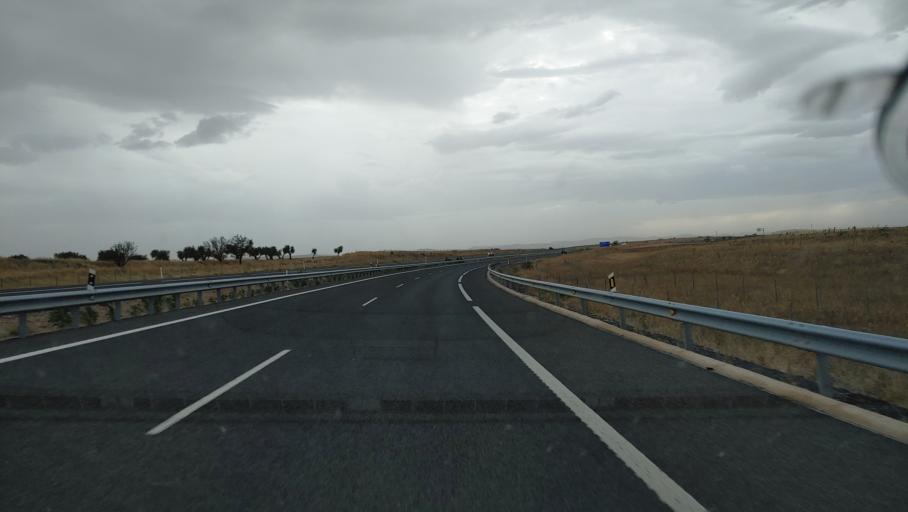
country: ES
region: Castille-La Mancha
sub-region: Provincia de Ciudad Real
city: Poblete
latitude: 38.9295
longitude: -3.9750
